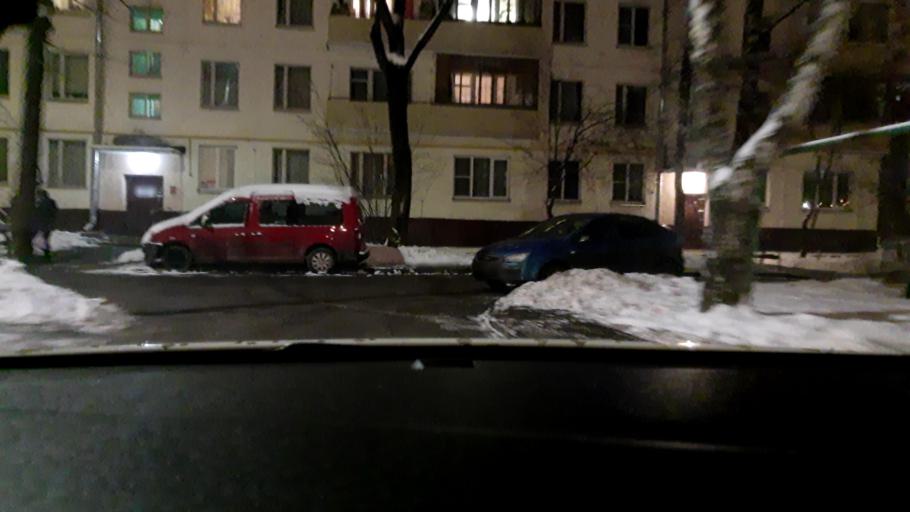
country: RU
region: Moscow
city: Strogino
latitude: 55.8553
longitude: 37.4145
